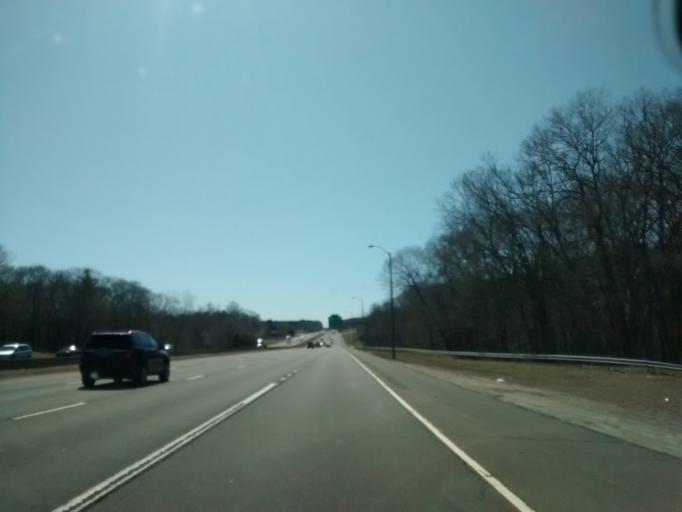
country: US
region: Connecticut
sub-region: Tolland County
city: Stafford Springs
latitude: 41.8917
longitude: -72.3005
